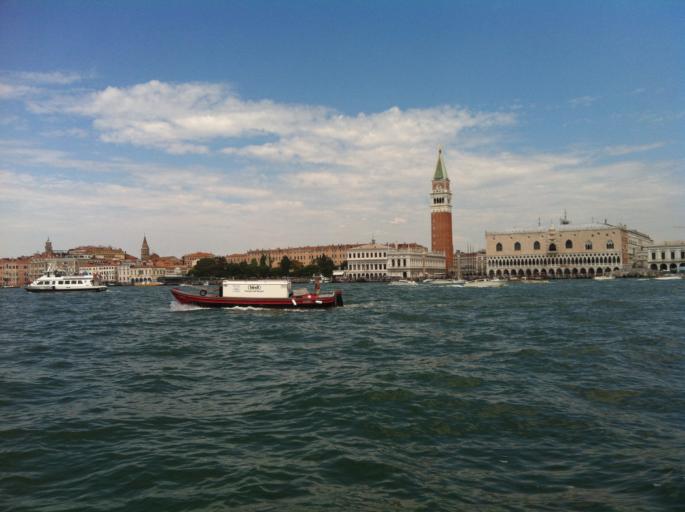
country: IT
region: Veneto
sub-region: Provincia di Venezia
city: Venice
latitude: 45.4305
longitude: 12.3426
